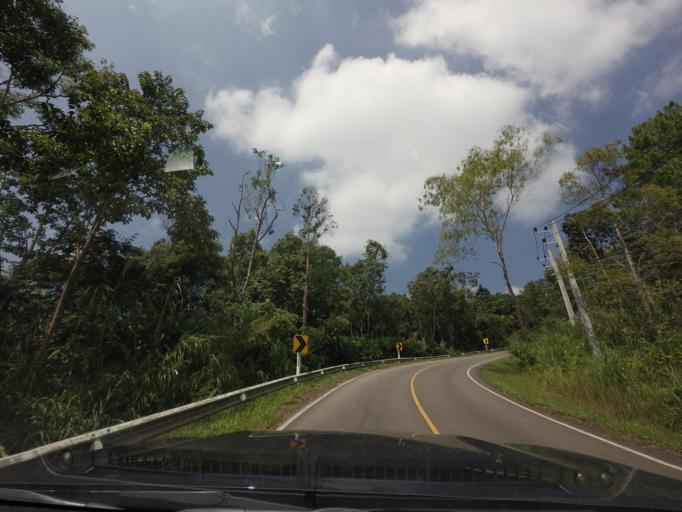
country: TH
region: Loei
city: Na Haeo
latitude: 17.4798
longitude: 100.9153
